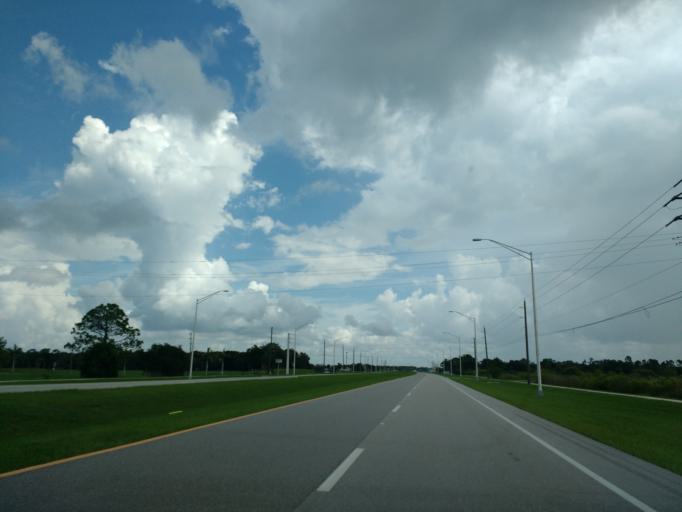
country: US
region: Florida
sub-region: Lee County
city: Burnt Store Marina
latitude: 26.7809
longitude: -82.0379
